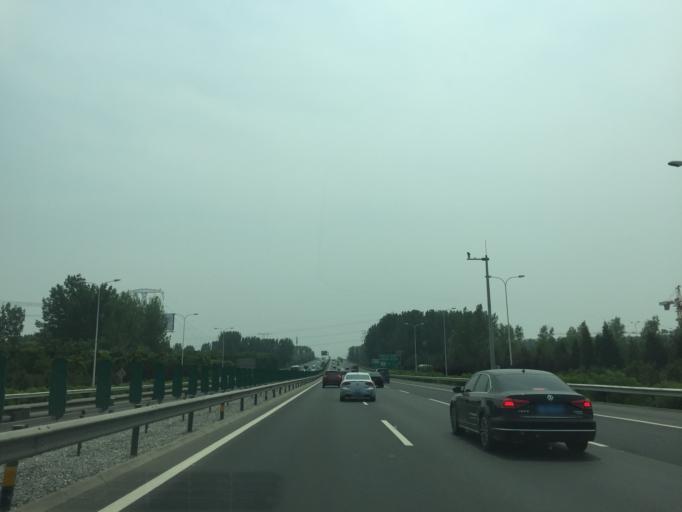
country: CN
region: Beijing
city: Gaoliying
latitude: 40.1278
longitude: 116.4775
